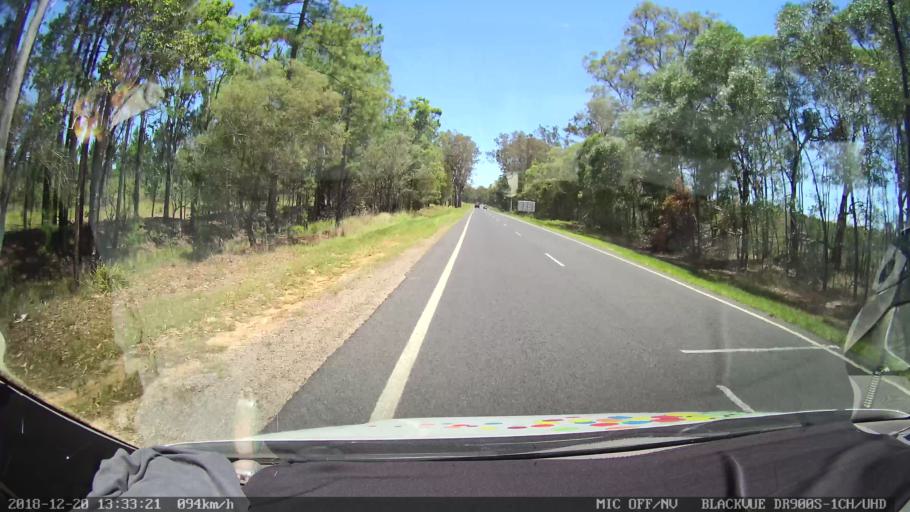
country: AU
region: New South Wales
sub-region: Clarence Valley
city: Gordon
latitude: -29.2441
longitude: 152.9869
